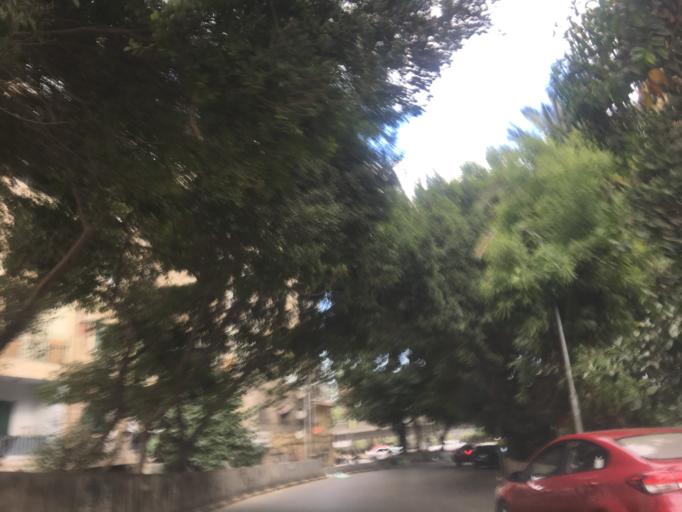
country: EG
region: Muhafazat al Qahirah
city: Cairo
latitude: 30.0488
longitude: 31.2168
